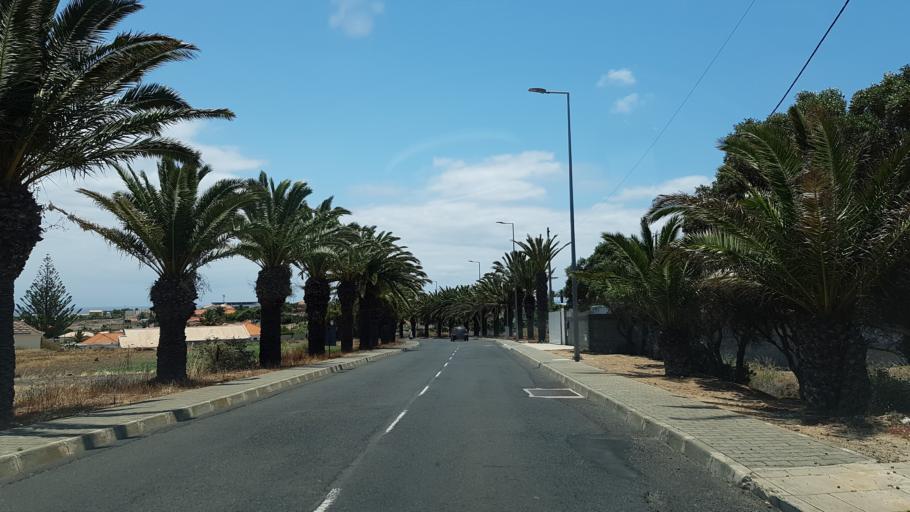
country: PT
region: Madeira
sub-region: Porto Santo
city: Vila de Porto Santo
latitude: 33.0685
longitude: -16.3444
